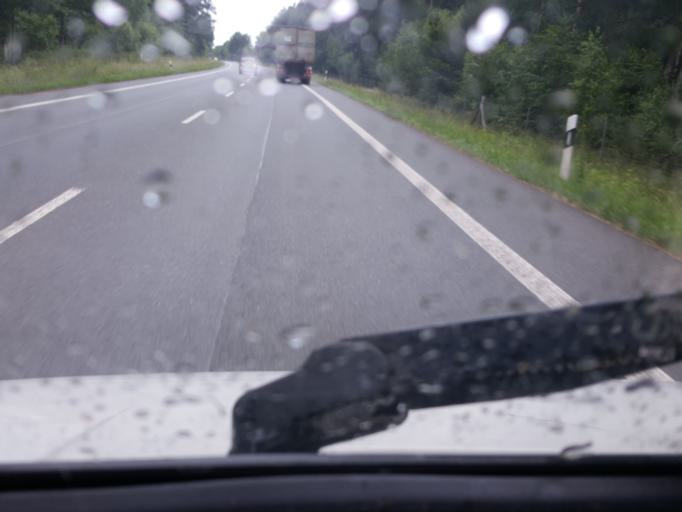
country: DE
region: North Rhine-Westphalia
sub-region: Regierungsbezirk Detmold
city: Petershagen
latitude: 52.3633
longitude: 8.9584
